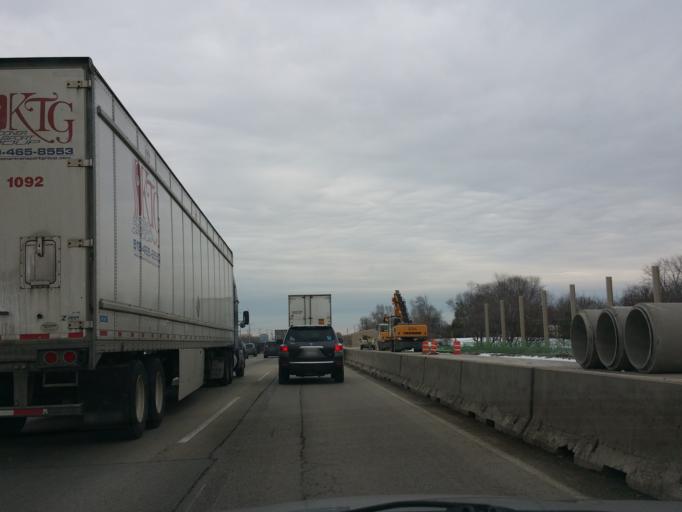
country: US
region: Illinois
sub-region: Cook County
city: Hoffman Estates
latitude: 42.0662
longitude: -88.0989
